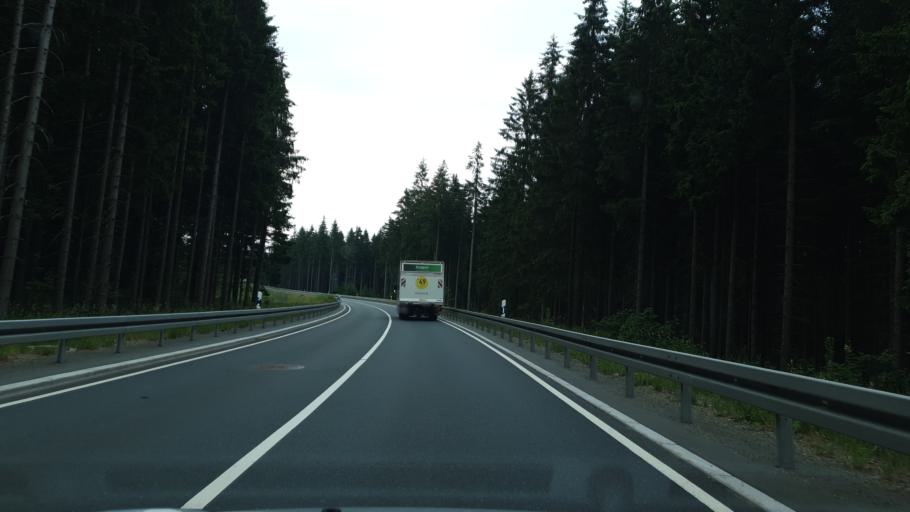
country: DE
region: Saxony
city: Hammerbrucke
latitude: 50.4695
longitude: 12.4329
